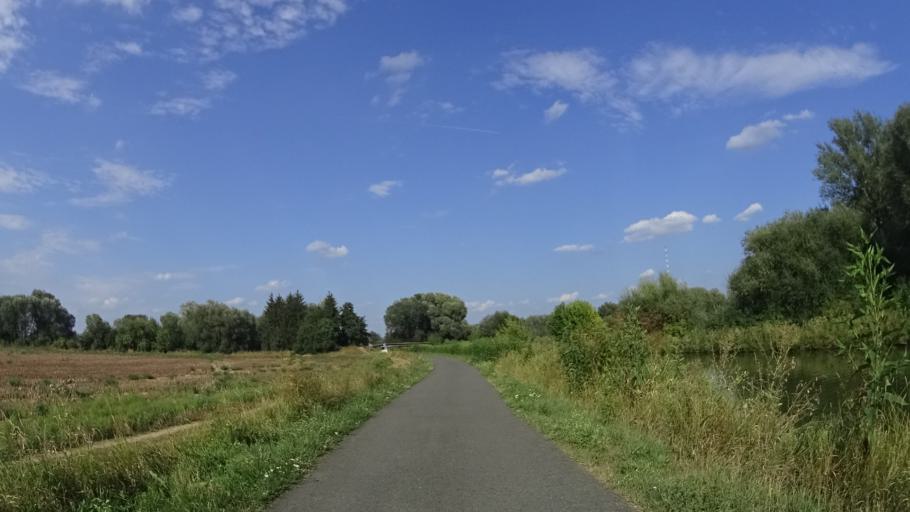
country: CZ
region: Zlin
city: Babice
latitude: 49.1239
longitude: 17.4908
